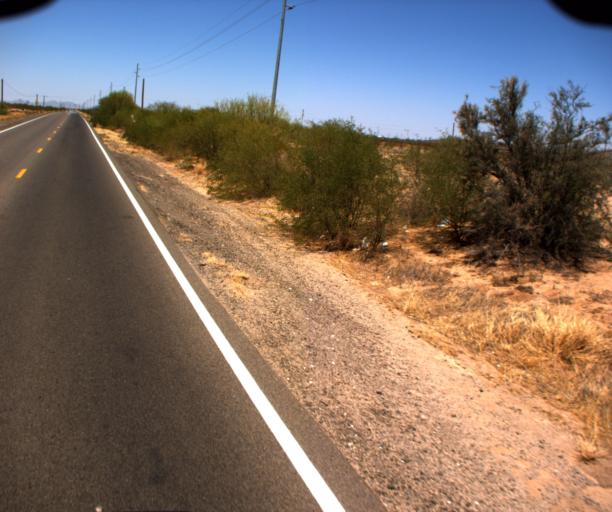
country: US
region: Arizona
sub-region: Pinal County
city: Maricopa
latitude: 33.0732
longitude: -112.1920
